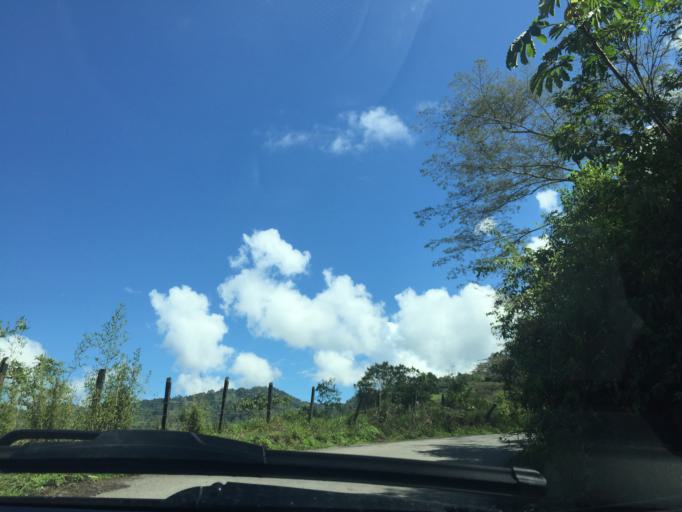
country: CO
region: Cundinamarca
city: San Francisco
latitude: 4.9955
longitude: -74.2853
